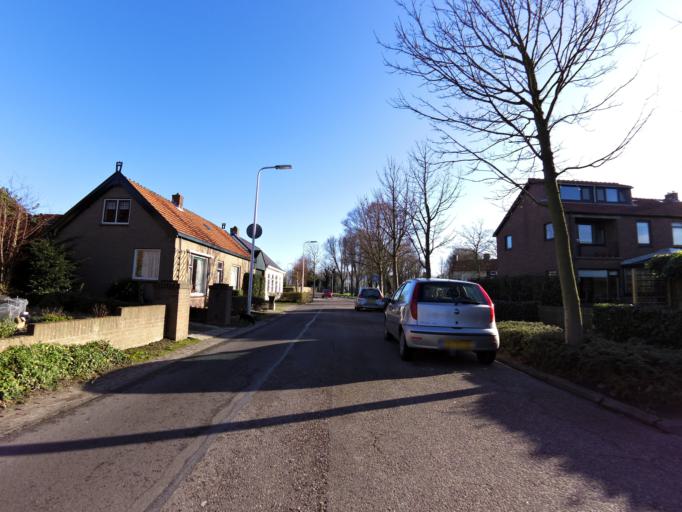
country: NL
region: South Holland
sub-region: Gemeente Hellevoetsluis
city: Nieuw-Helvoet
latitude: 51.8737
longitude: 4.0748
